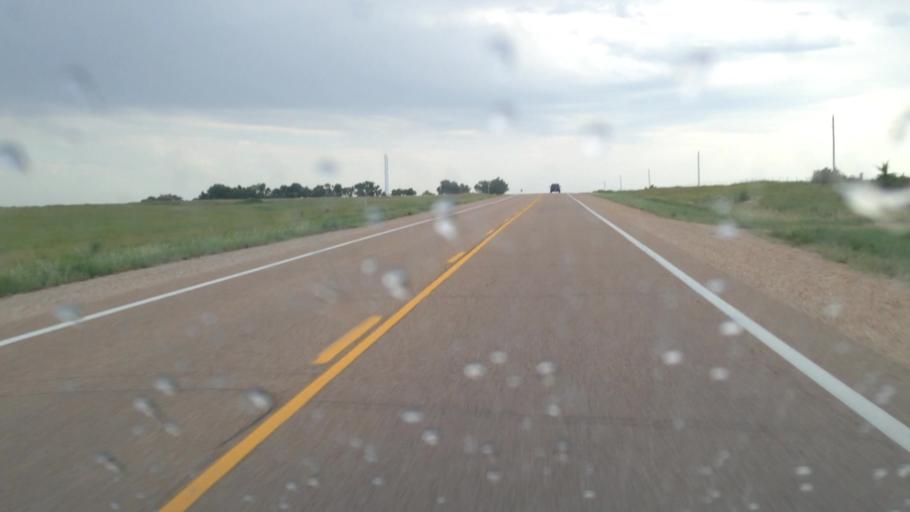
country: US
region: Kansas
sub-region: Coffey County
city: Burlington
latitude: 38.1458
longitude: -95.7392
